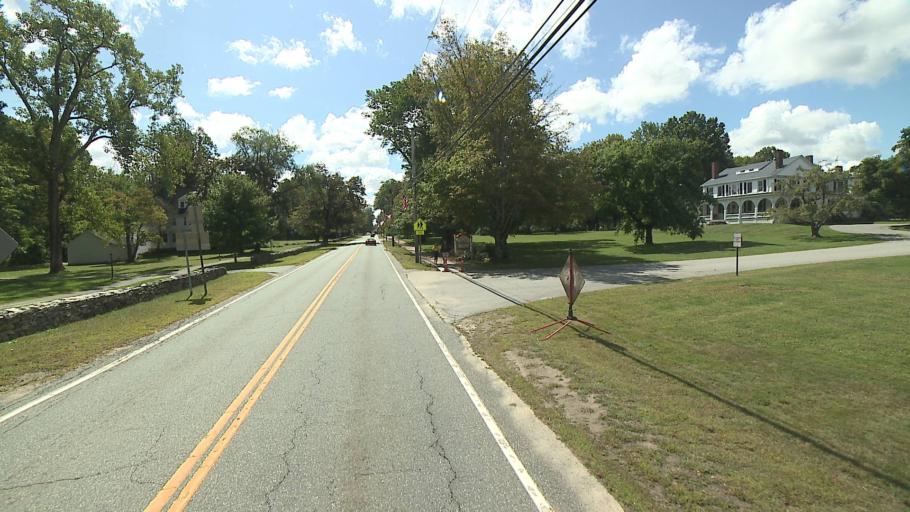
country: US
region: Connecticut
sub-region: Windham County
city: South Woodstock
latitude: 41.8967
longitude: -71.9621
